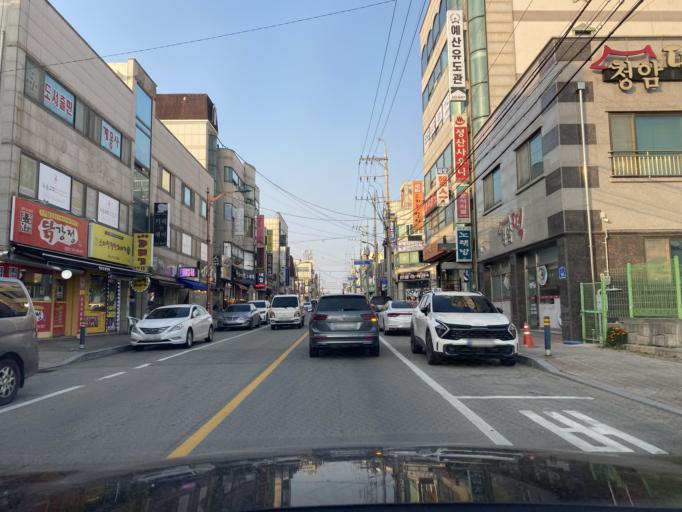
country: KR
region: Chungcheongnam-do
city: Yesan
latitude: 36.6909
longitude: 126.8301
